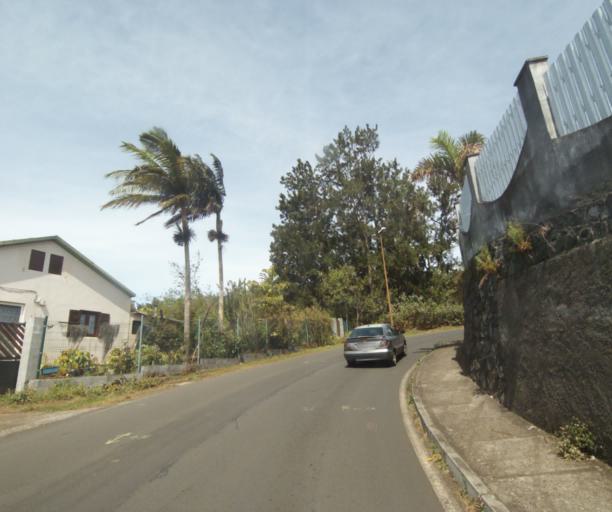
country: RE
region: Reunion
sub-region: Reunion
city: Saint-Paul
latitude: -21.0386
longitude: 55.3170
